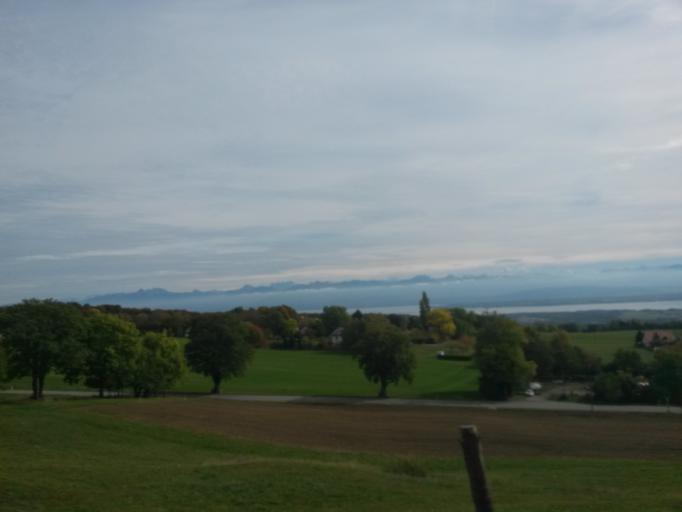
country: CH
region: Vaud
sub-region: Nyon District
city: Arzier
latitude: 46.4586
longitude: 6.2201
